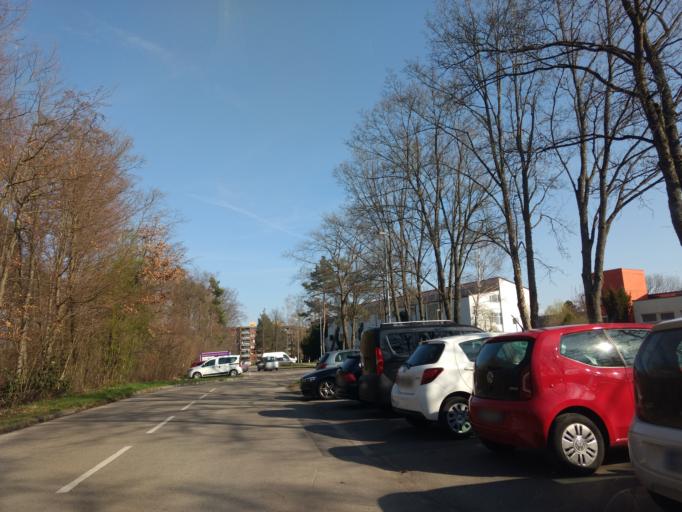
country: DE
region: Baden-Wuerttemberg
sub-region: Regierungsbezirk Stuttgart
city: Filderstadt
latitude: 48.6544
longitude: 9.1879
